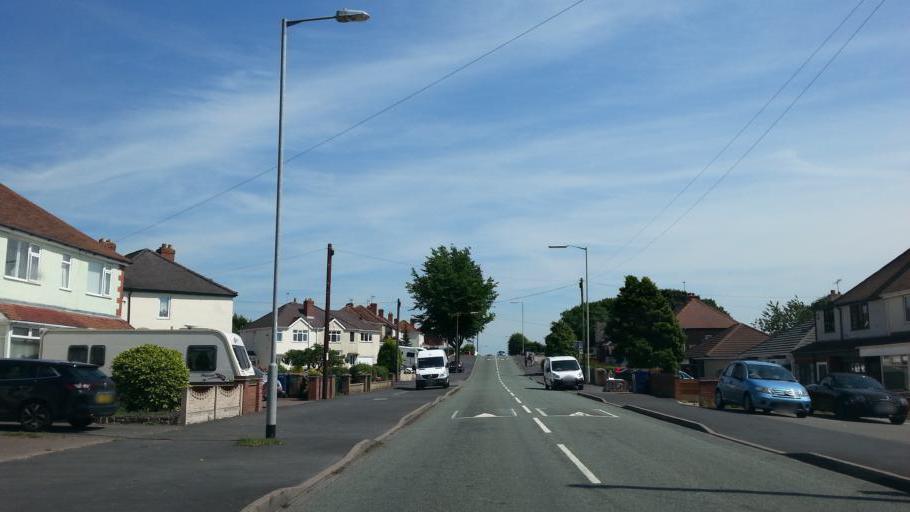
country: GB
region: England
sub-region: Staffordshire
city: Cannock
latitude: 52.7101
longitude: -2.0162
